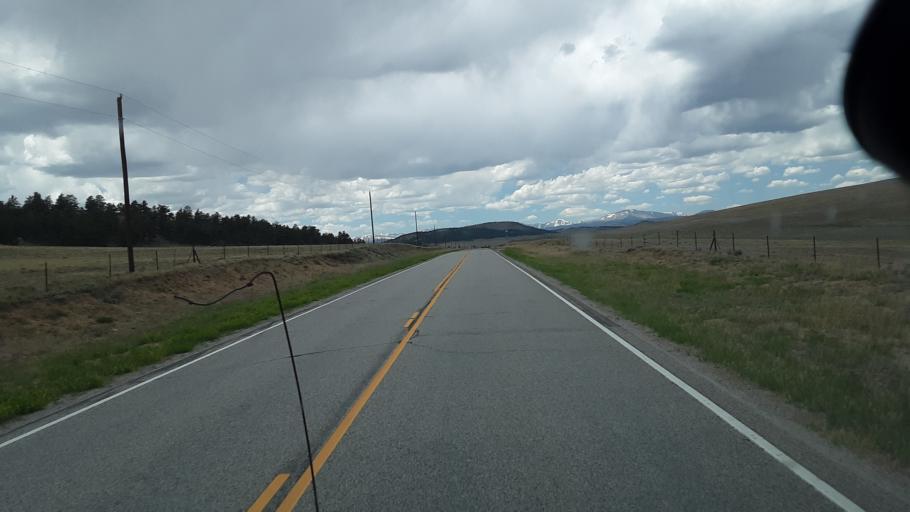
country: US
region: Colorado
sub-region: Park County
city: Fairplay
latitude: 39.0065
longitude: -105.7788
